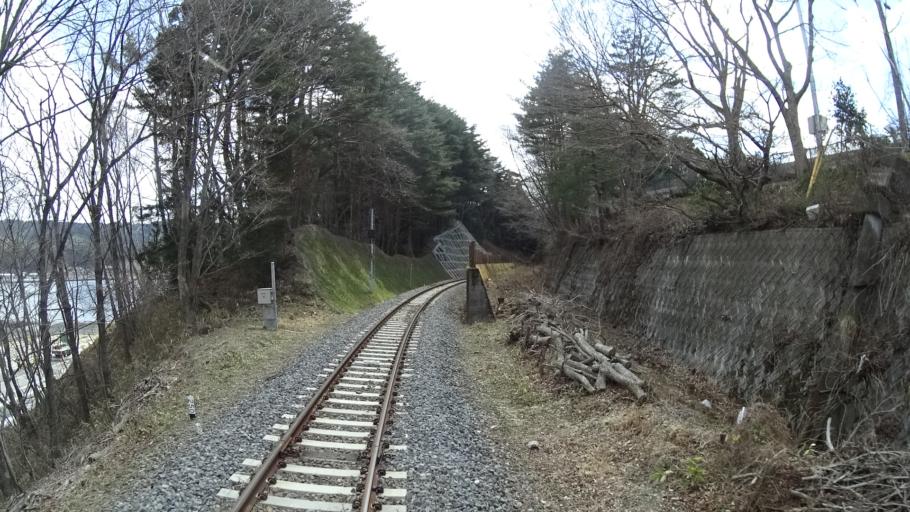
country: JP
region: Iwate
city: Otsuchi
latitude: 39.3759
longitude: 141.9415
